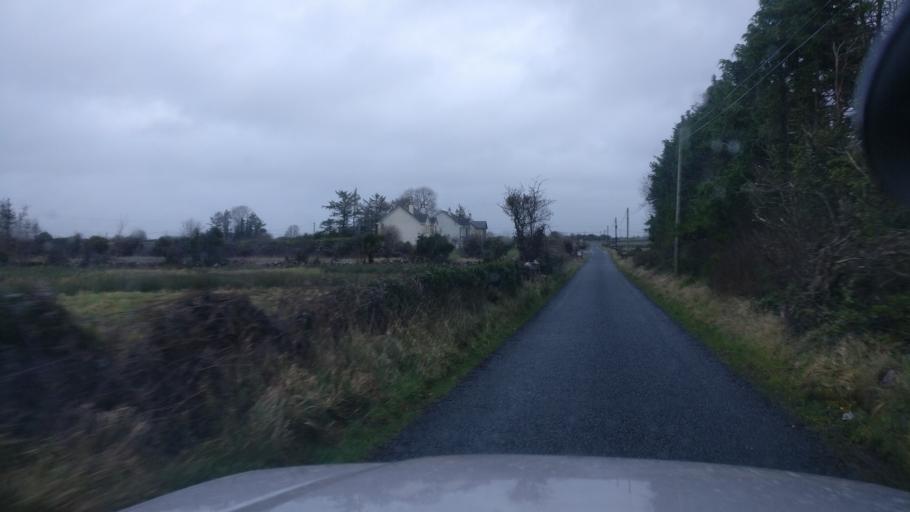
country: IE
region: Connaught
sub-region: County Galway
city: Loughrea
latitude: 53.2161
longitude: -8.6245
